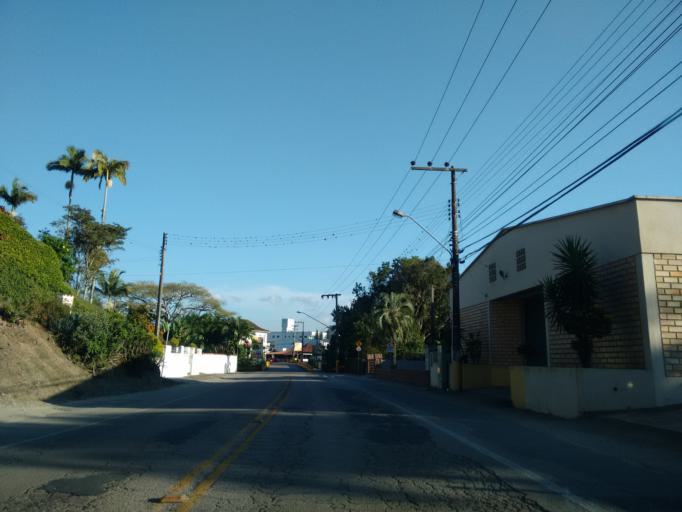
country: BR
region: Santa Catarina
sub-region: Gaspar
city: Gaspar
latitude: -26.9261
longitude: -48.9524
